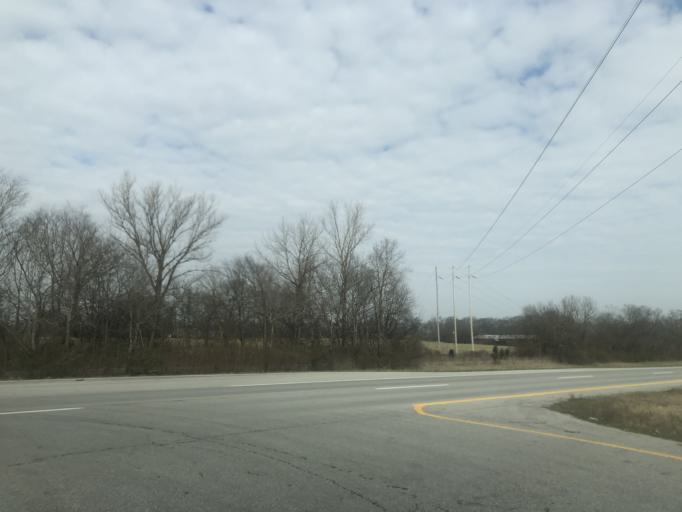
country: US
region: Tennessee
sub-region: Maury County
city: Mount Pleasant
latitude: 35.5523
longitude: -87.2068
